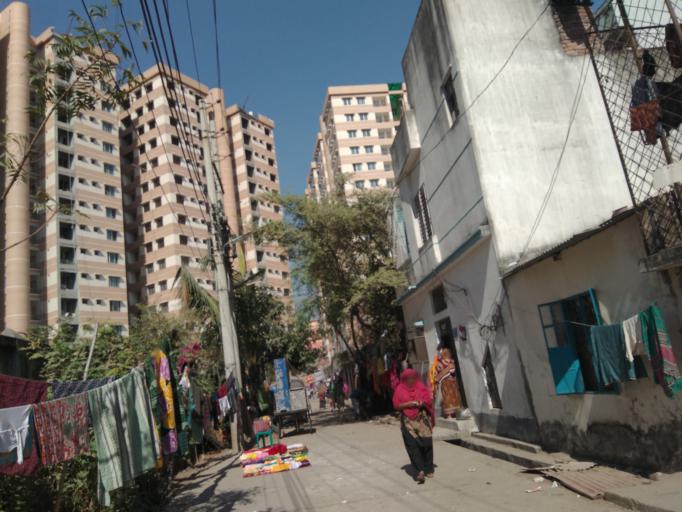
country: BD
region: Dhaka
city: Azimpur
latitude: 23.7705
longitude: 90.3603
